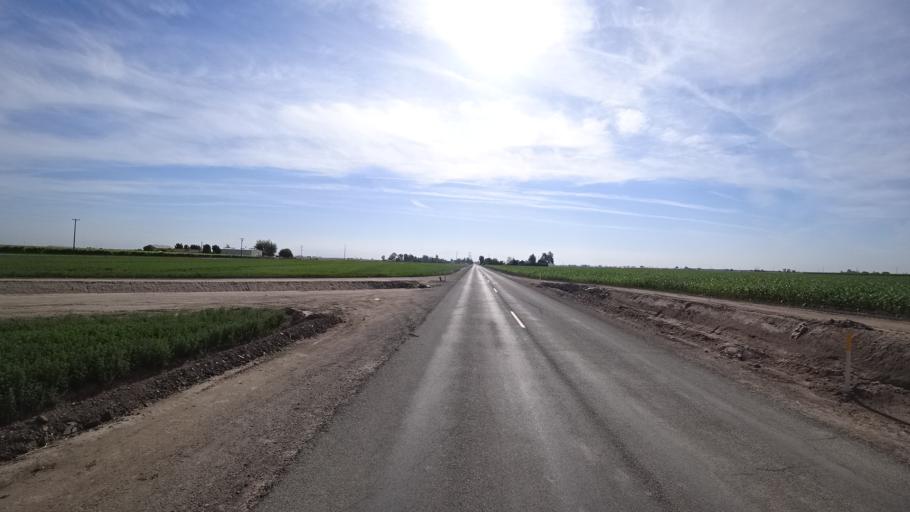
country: US
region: California
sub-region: Tulare County
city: Goshen
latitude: 36.3492
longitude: -119.4842
